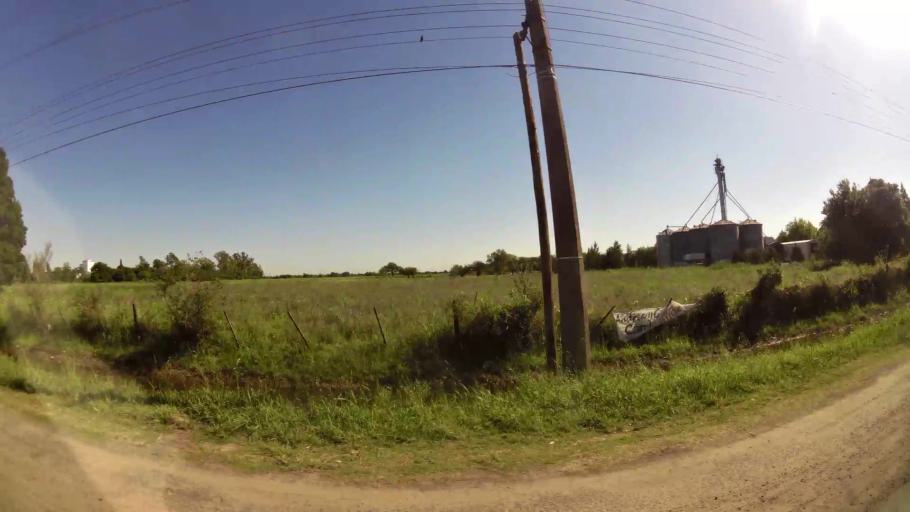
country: AR
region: Santa Fe
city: Esperanza
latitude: -31.4479
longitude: -60.9076
